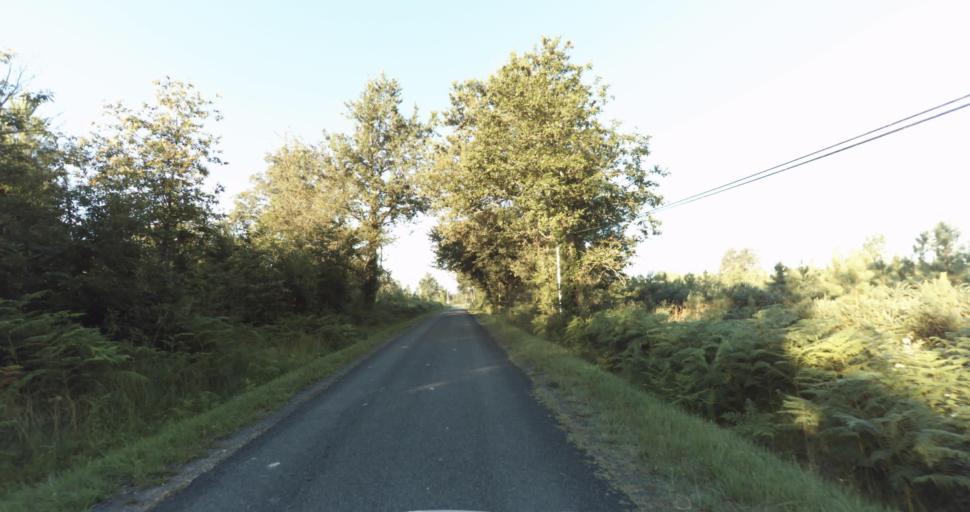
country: FR
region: Aquitaine
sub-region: Departement de la Gironde
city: Bazas
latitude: 44.4097
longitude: -0.2442
